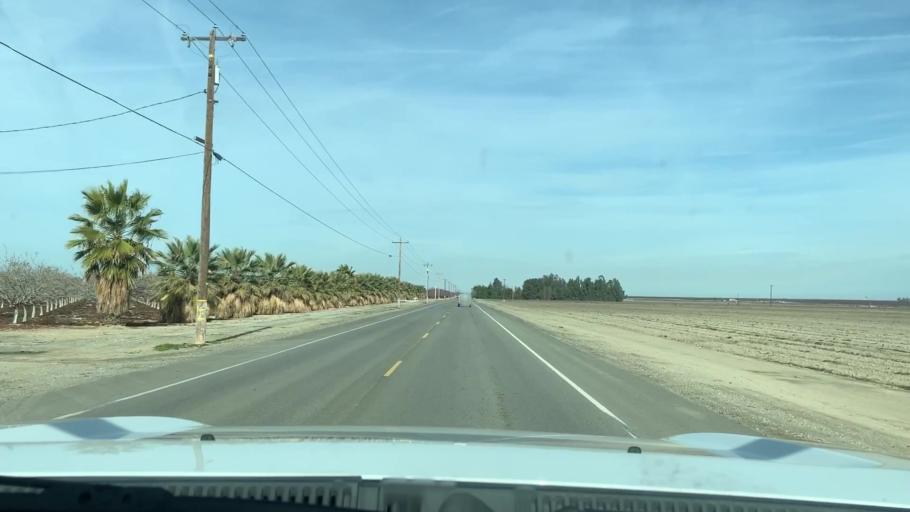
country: US
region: California
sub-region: Kern County
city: Buttonwillow
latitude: 35.5045
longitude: -119.4747
